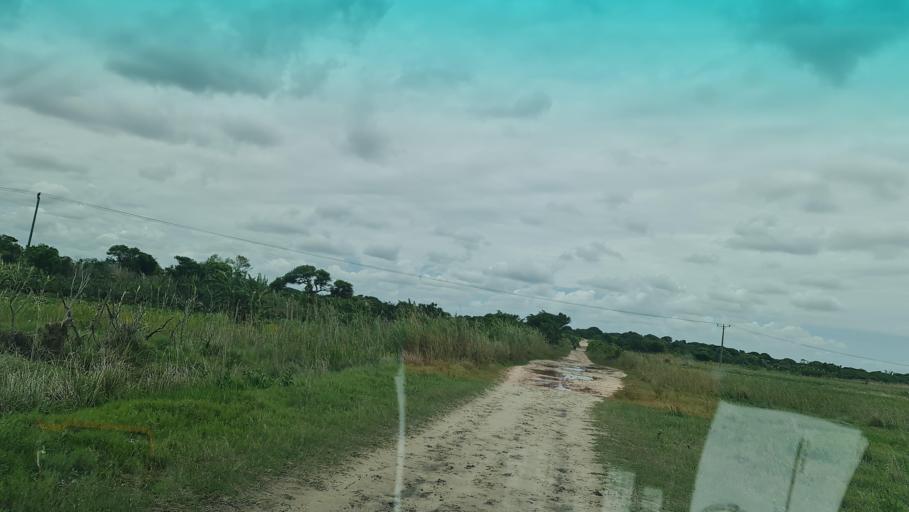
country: MZ
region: Maputo City
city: Maputo
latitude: -25.7013
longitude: 32.7047
